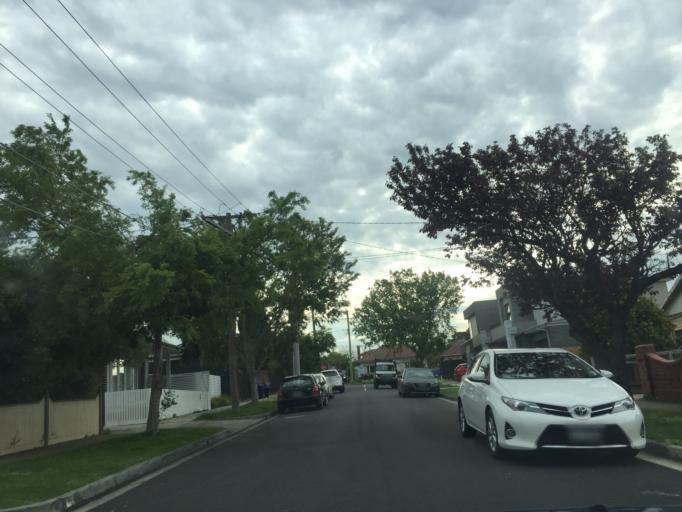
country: AU
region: Victoria
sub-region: Darebin
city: Preston
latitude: -37.7523
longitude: 145.0120
